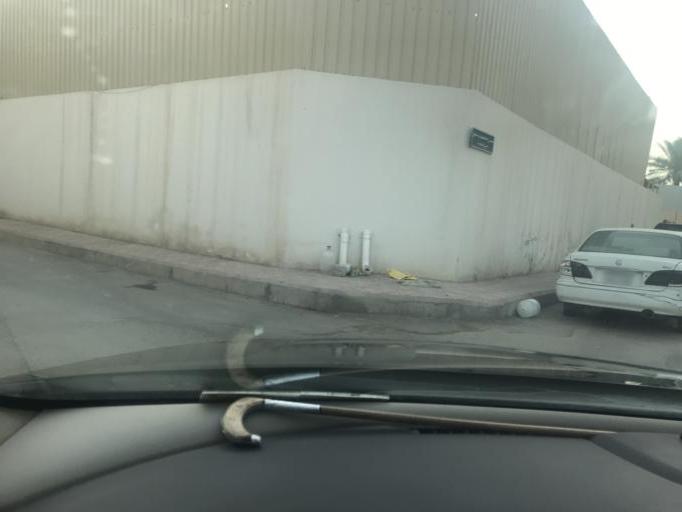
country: SA
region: Ar Riyad
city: Riyadh
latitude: 24.7373
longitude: 46.7781
